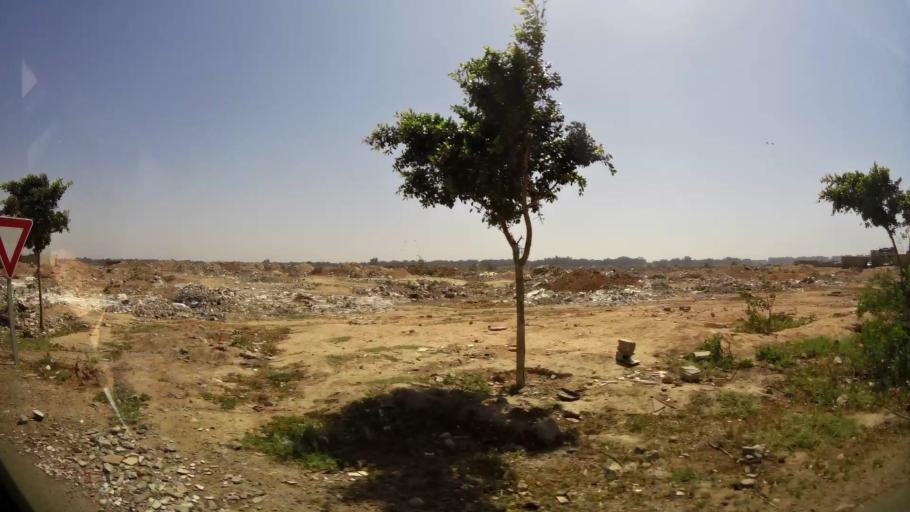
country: MA
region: Souss-Massa-Draa
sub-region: Inezgane-Ait Mellou
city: Inezgane
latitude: 30.3434
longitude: -9.5439
